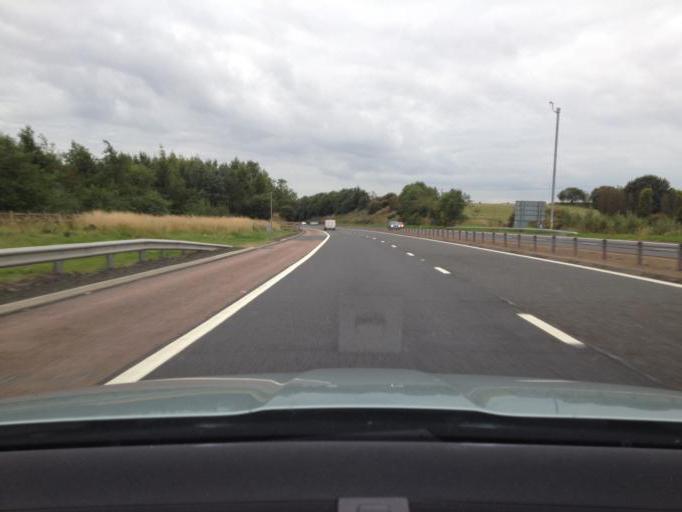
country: GB
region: Scotland
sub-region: Fife
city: Crossgates
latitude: 56.0920
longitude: -3.4009
